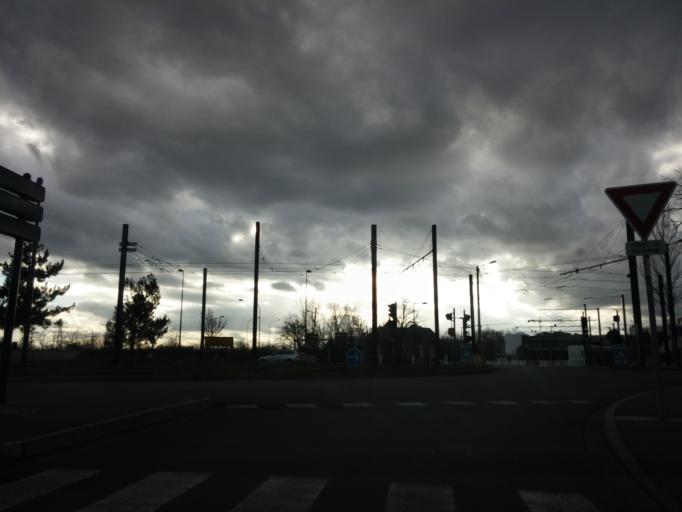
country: FR
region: Midi-Pyrenees
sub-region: Departement de la Haute-Garonne
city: Blagnac
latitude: 43.6220
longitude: 1.3971
